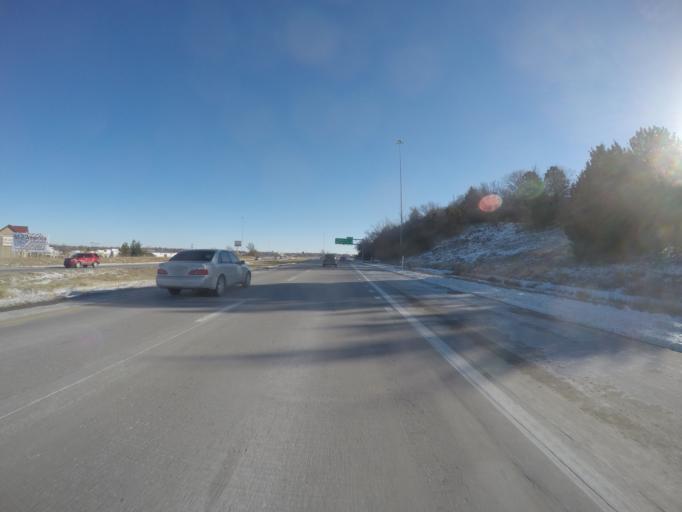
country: US
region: Kansas
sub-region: Shawnee County
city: Topeka
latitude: 39.0465
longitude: -95.7689
